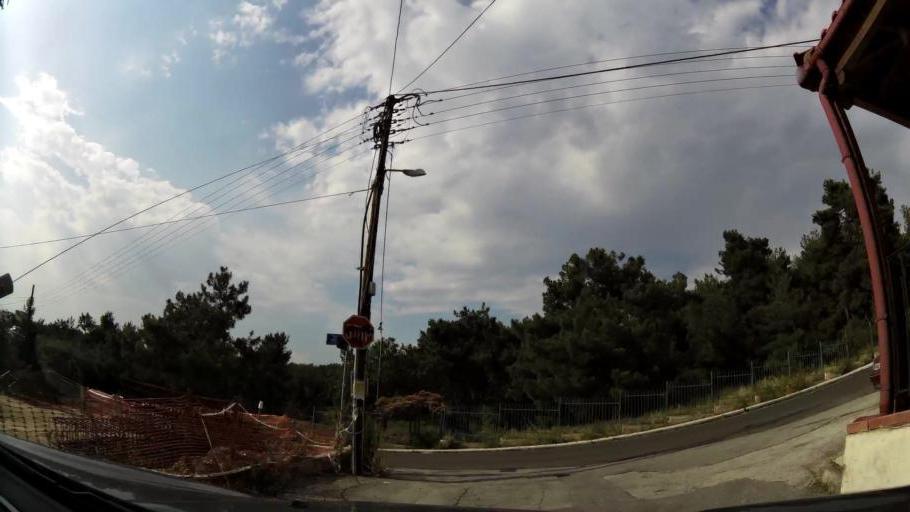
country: GR
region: Central Macedonia
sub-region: Nomos Thessalonikis
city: Polichni
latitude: 40.6613
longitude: 22.9584
